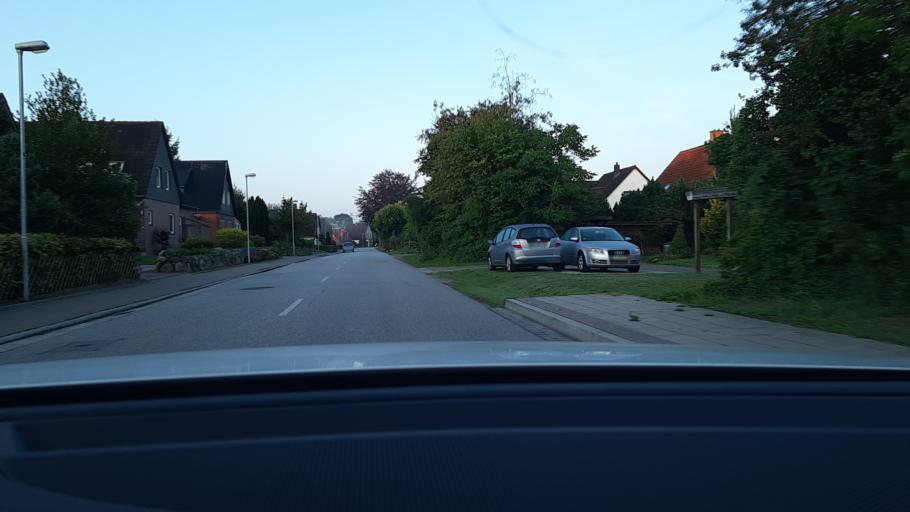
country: DE
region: Schleswig-Holstein
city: Hamberge
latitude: 53.8284
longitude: 10.6038
